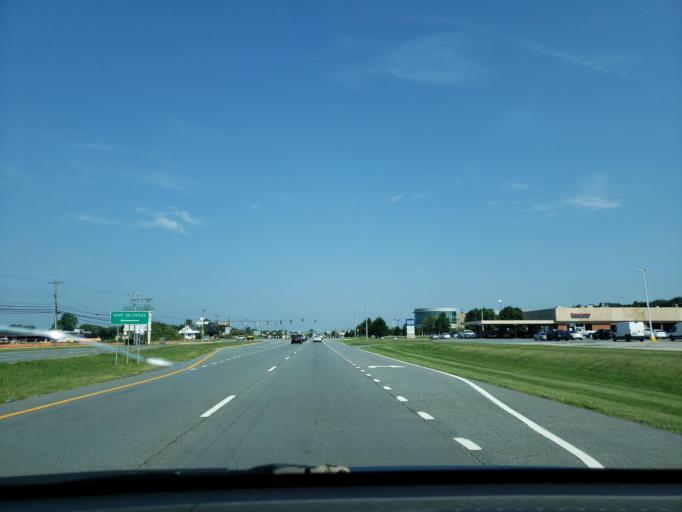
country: US
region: Delaware
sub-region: Kent County
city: Dover
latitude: 39.1521
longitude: -75.5054
